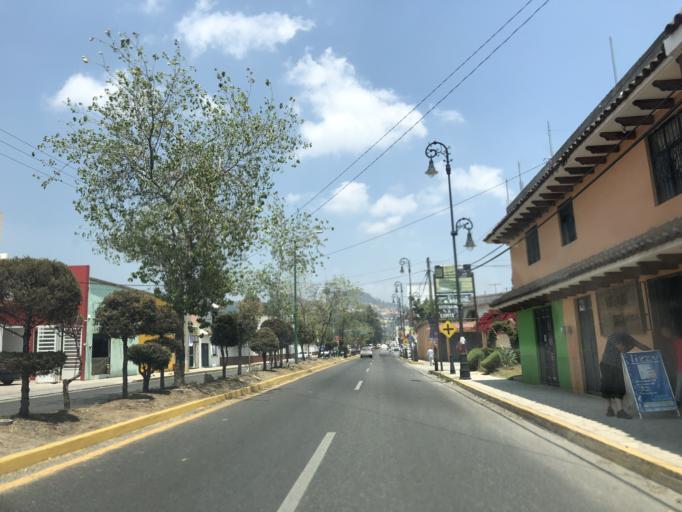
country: MX
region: Chiapas
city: San Cristobal de las Casas
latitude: 16.7215
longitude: -92.6442
